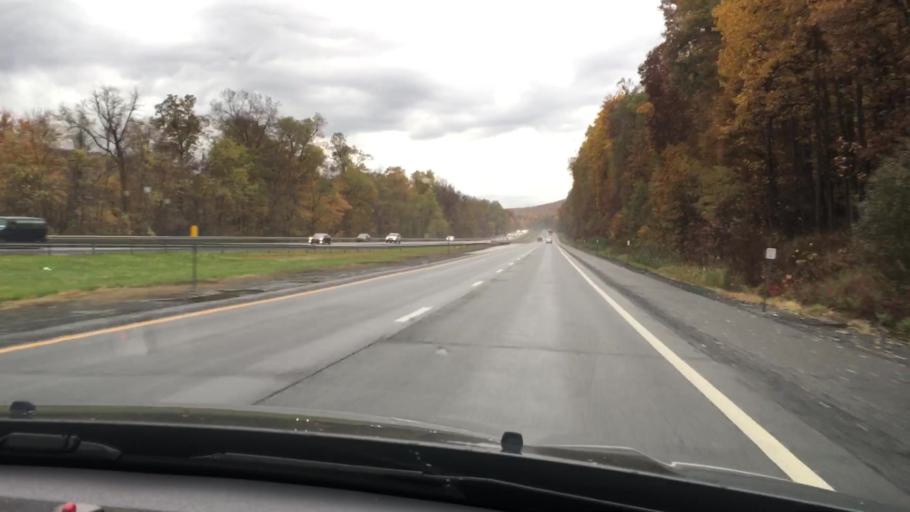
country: US
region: New York
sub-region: Orange County
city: Woodbury
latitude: 41.3936
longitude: -74.0938
